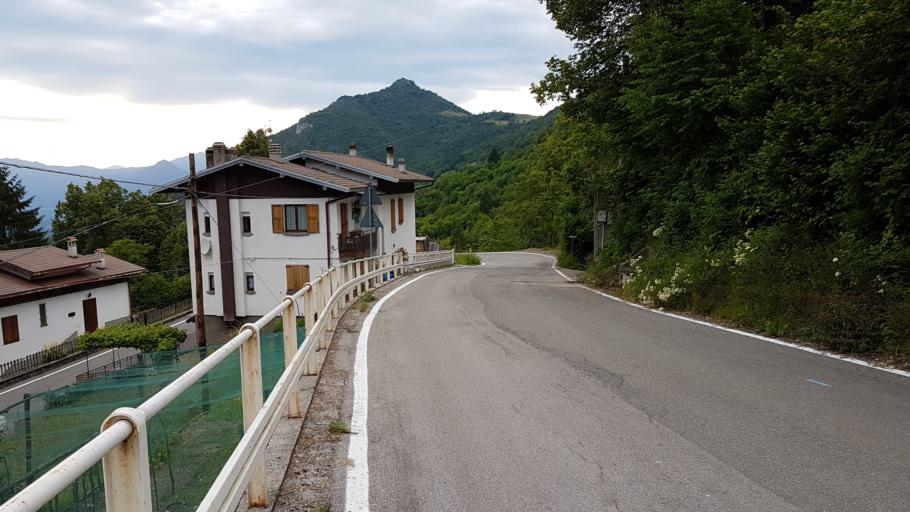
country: IT
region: Lombardy
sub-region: Provincia di Lecco
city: Esino Lario
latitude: 45.9932
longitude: 9.3411
